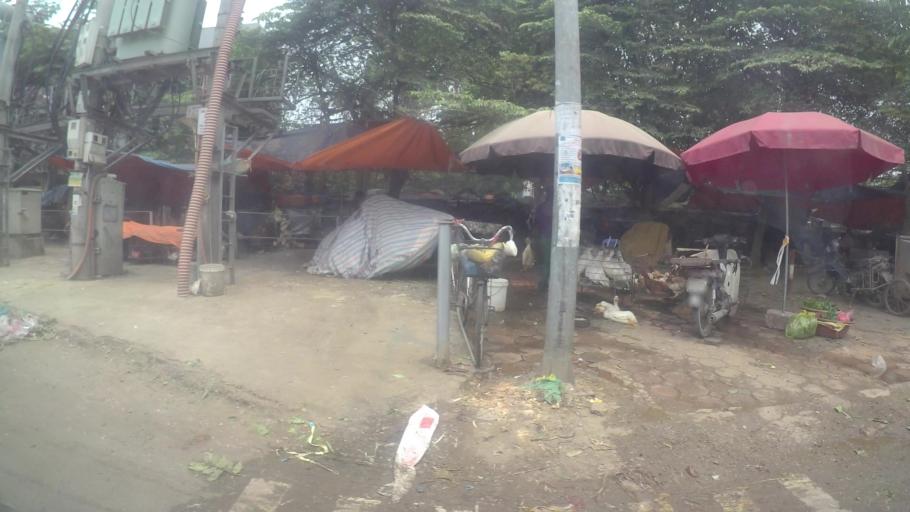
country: VN
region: Ha Noi
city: Ha Dong
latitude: 20.9782
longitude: 105.7465
